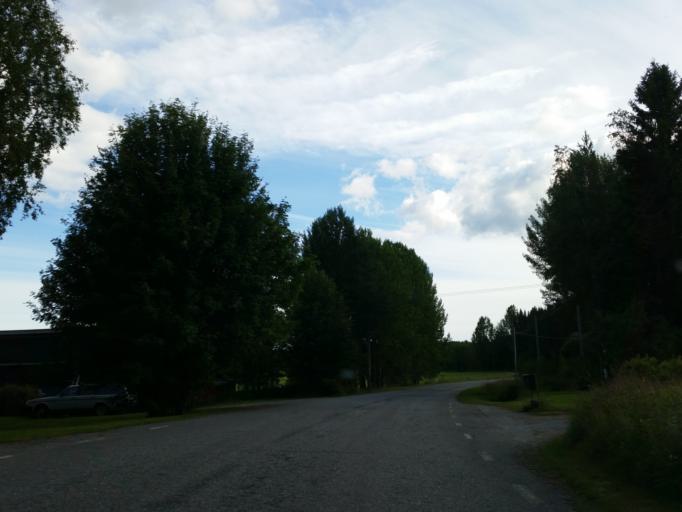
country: SE
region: Vaesterbotten
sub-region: Robertsfors Kommun
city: Robertsfors
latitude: 64.0530
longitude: 20.8548
